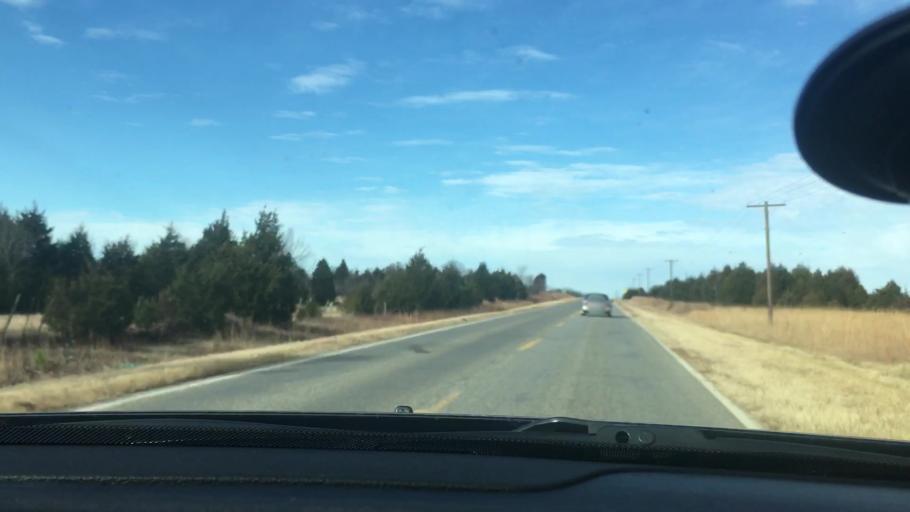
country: US
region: Oklahoma
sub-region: Seminole County
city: Konawa
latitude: 34.9447
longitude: -96.7234
